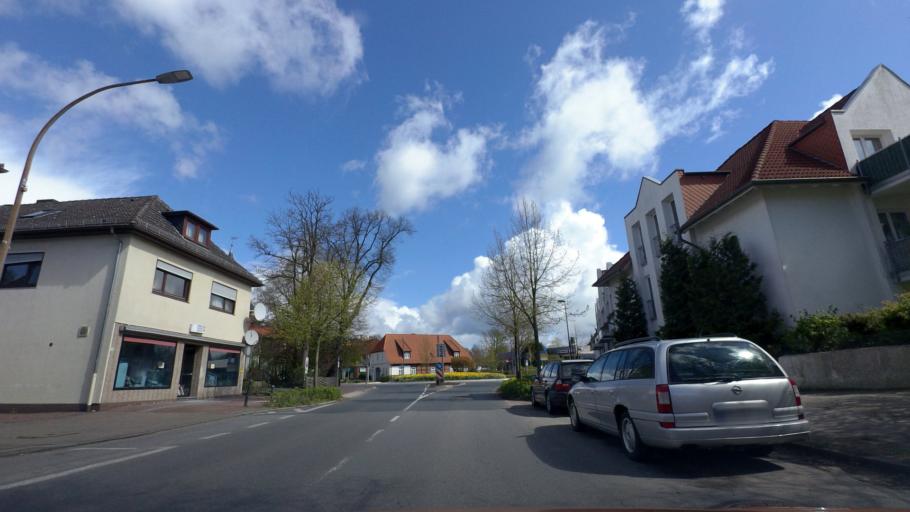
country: DE
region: Lower Saxony
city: Ottersberg
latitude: 53.1080
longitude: 9.1422
